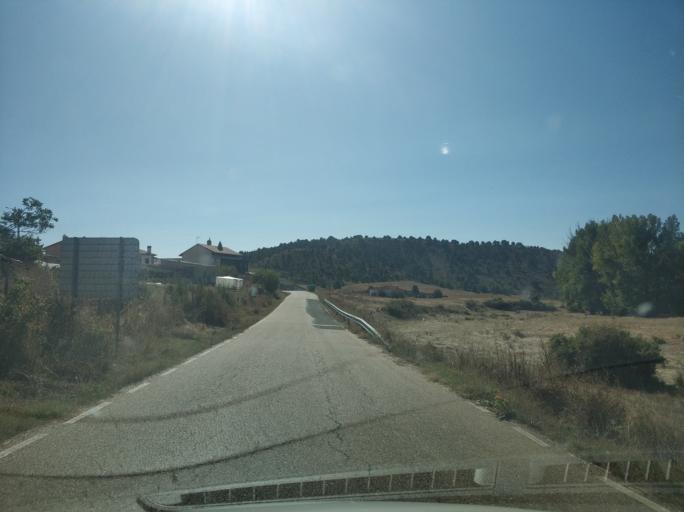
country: ES
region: Castille and Leon
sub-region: Provincia de Soria
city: Santa Maria de las Hoyas
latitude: 41.7715
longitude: -3.1715
